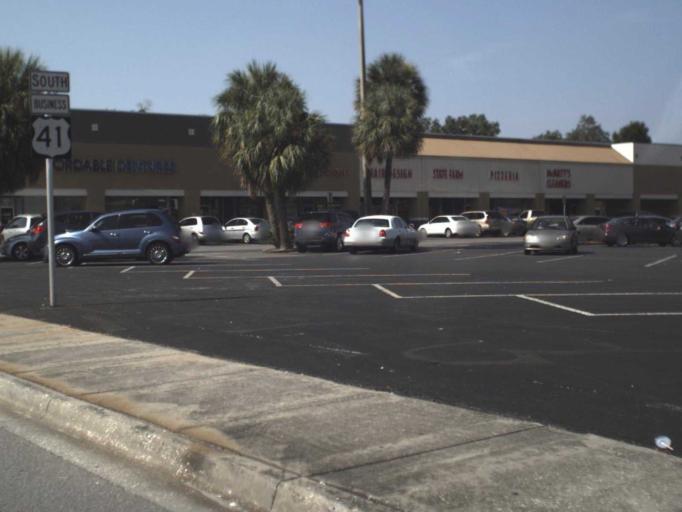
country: US
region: Florida
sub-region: Hillsborough County
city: Lake Magdalene
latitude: 28.0872
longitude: -82.4597
